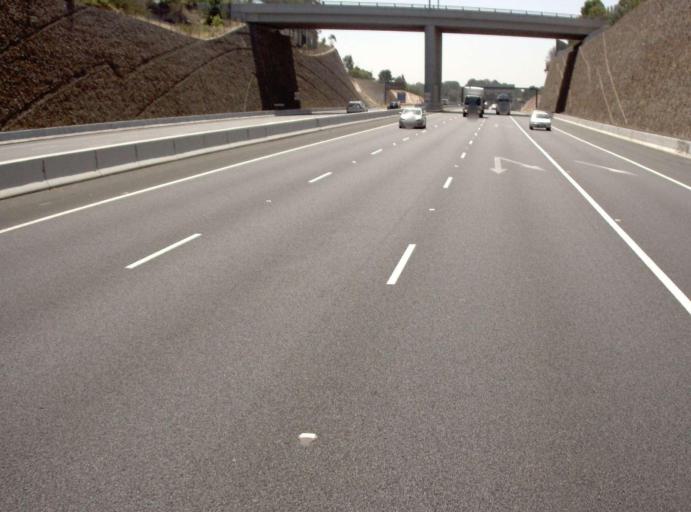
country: AU
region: Victoria
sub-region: Manningham
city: Donvale
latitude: -37.8025
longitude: 145.1844
